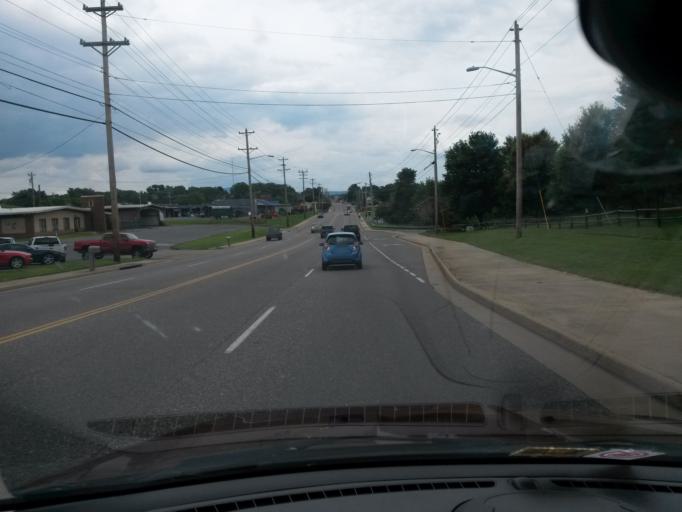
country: US
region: Virginia
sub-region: City of Harrisonburg
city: Harrisonburg
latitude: 38.4516
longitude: -78.8824
